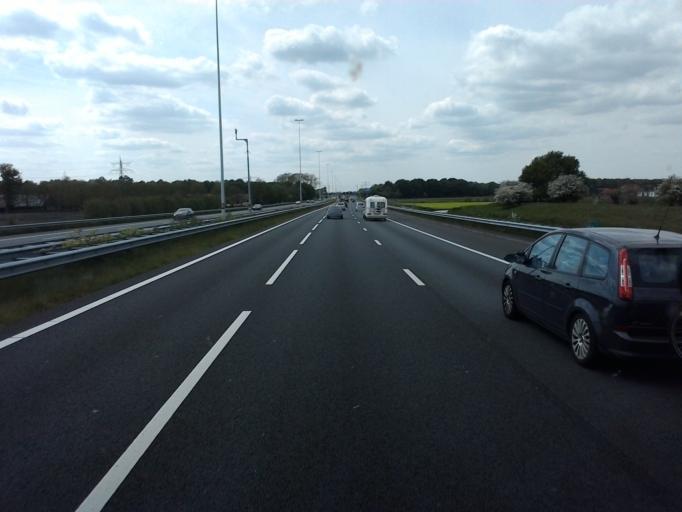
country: NL
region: Utrecht
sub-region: Gemeente Utrechtse Heuvelrug
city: Overberg
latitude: 52.0485
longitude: 5.4869
